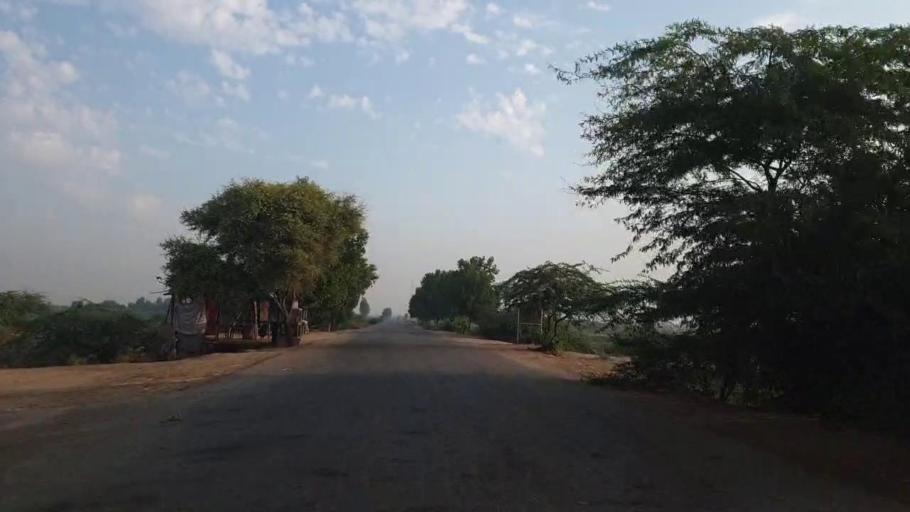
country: PK
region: Sindh
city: Badin
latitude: 24.6905
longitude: 68.9163
